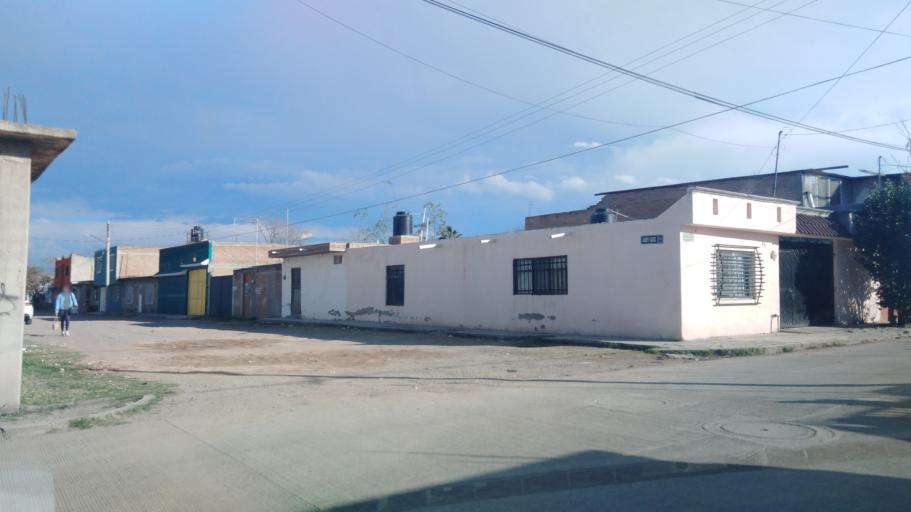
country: MX
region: Durango
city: Victoria de Durango
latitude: 24.0141
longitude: -104.6412
